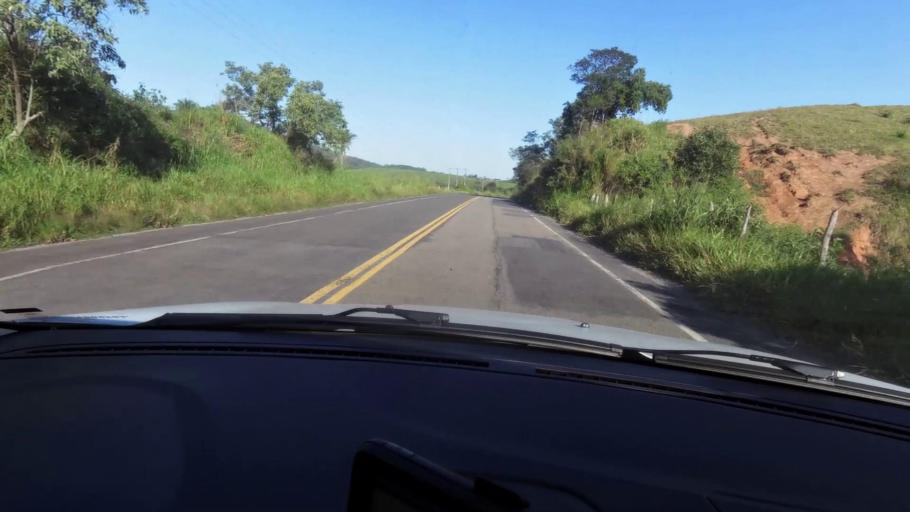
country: BR
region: Espirito Santo
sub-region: Piuma
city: Piuma
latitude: -20.7322
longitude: -40.6520
